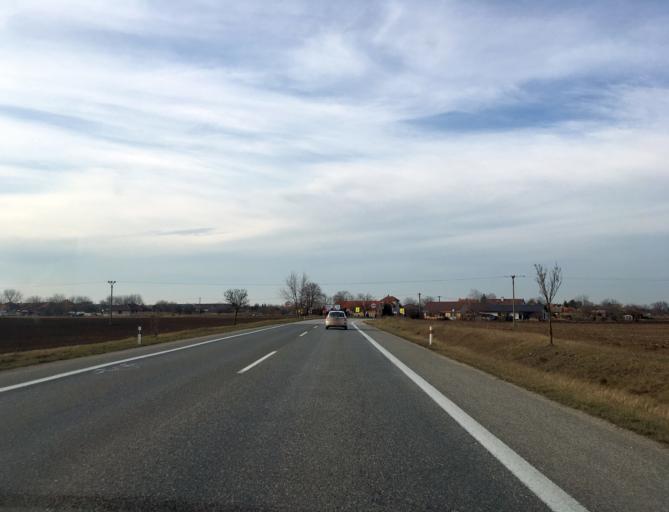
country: SK
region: Nitriansky
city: Sellye
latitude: 48.1221
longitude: 18.0321
